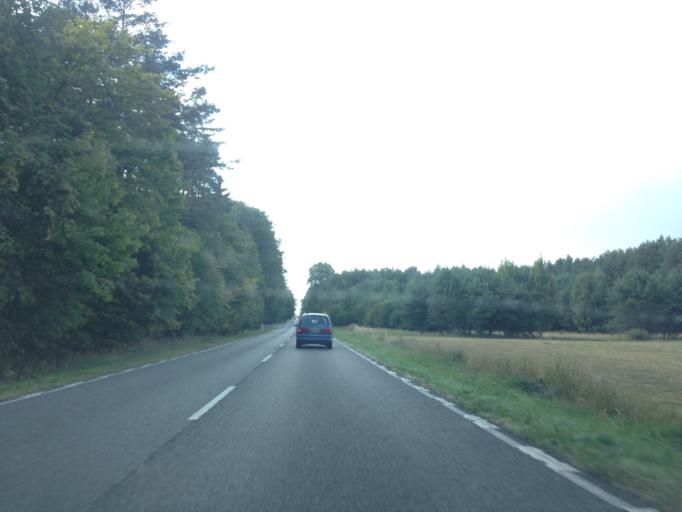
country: PL
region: Kujawsko-Pomorskie
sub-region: Powiat swiecki
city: Lniano
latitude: 53.4732
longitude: 18.1569
